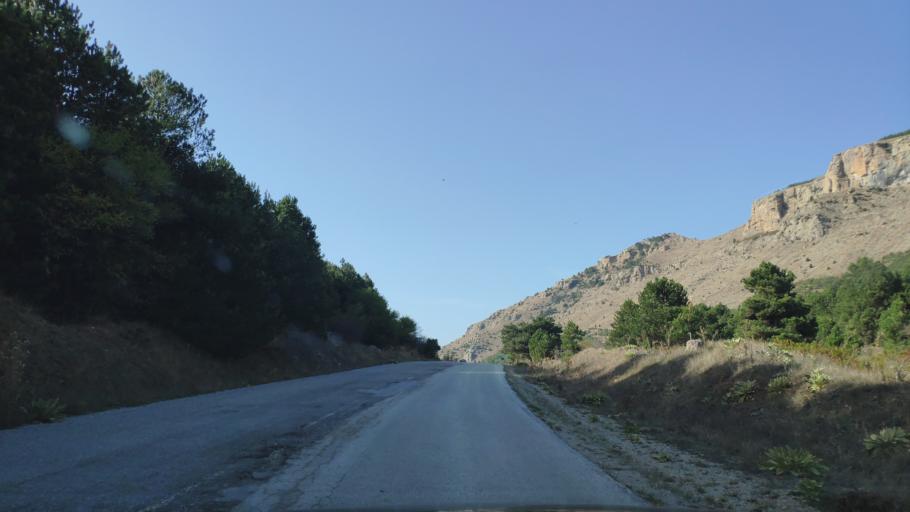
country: GR
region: West Greece
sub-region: Nomos Achaias
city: Aiyira
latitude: 38.0342
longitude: 22.4007
